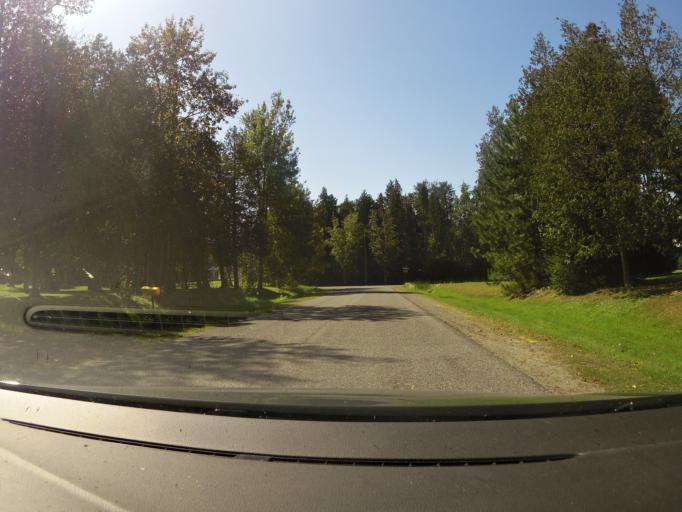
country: CA
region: Ontario
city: Bells Corners
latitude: 45.2765
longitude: -76.0117
